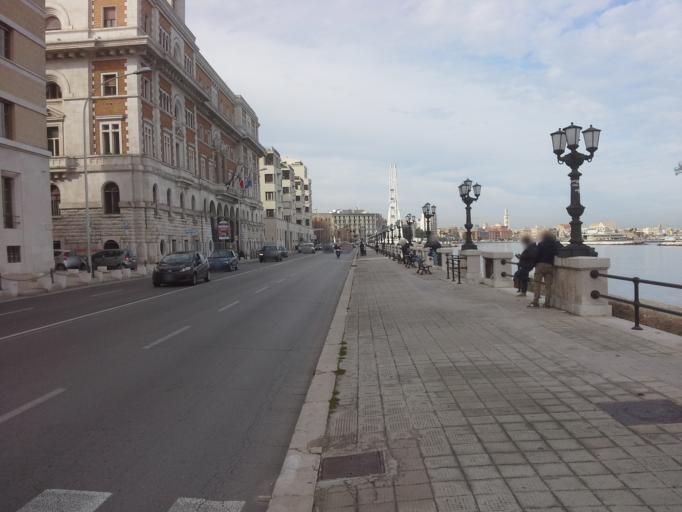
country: IT
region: Apulia
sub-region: Provincia di Bari
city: Bari
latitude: 41.1211
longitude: 16.8826
